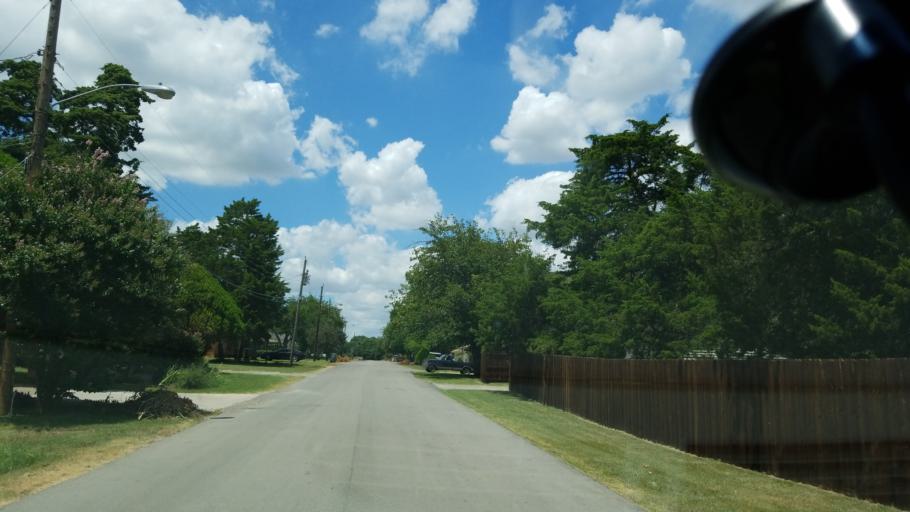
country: US
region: Texas
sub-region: Dallas County
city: Cockrell Hill
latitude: 32.6951
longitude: -96.8728
